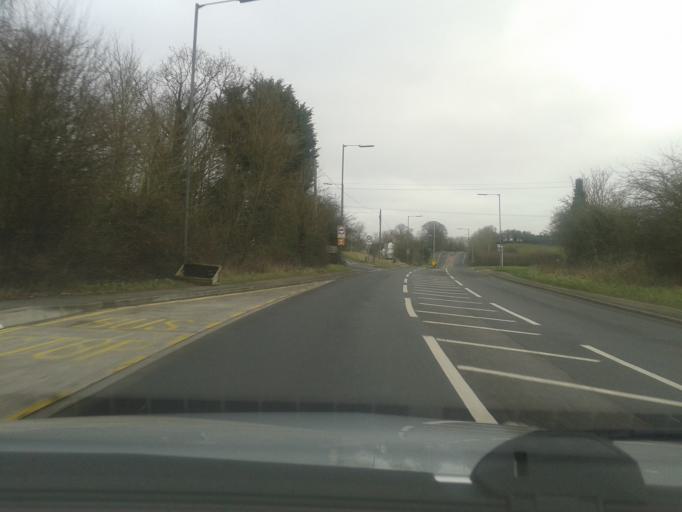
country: GB
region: England
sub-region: South Gloucestershire
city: Winterbourne
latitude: 51.5154
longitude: -2.4853
